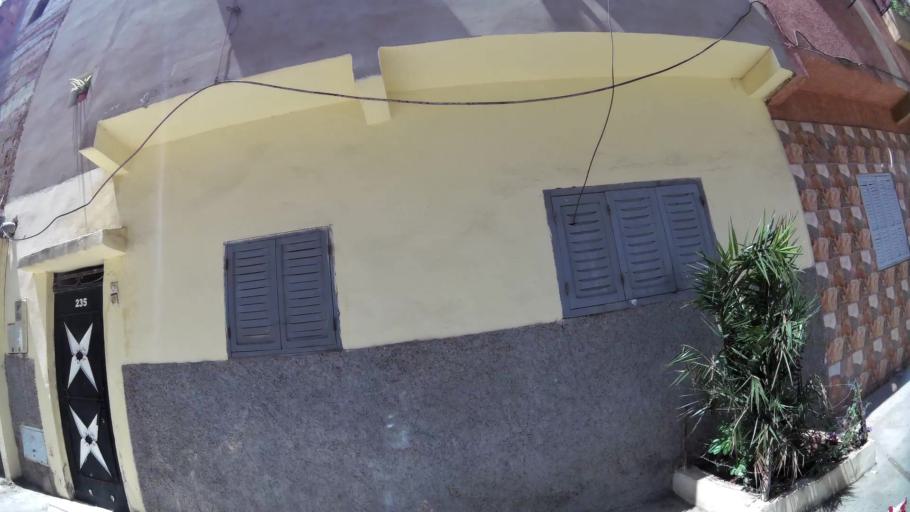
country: MA
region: Rabat-Sale-Zemmour-Zaer
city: Sale
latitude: 34.0667
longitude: -6.7876
